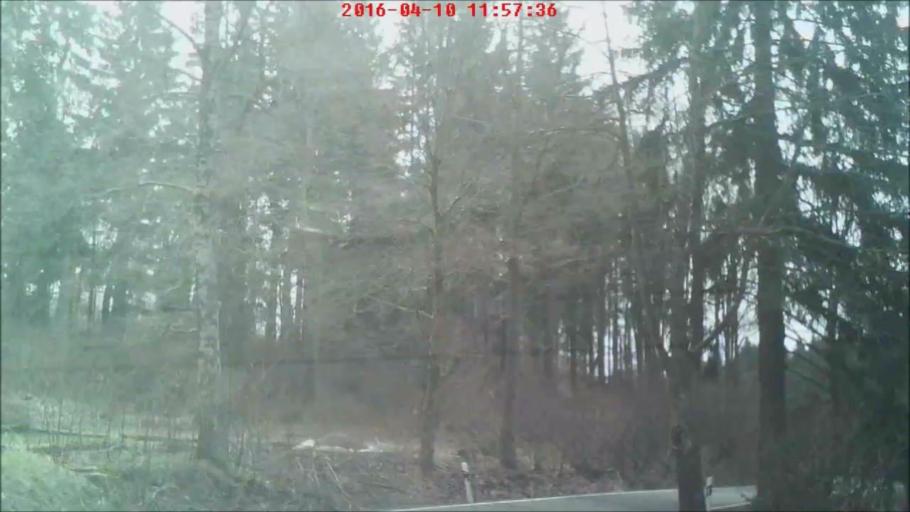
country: DE
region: Thuringia
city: Zella-Mehlis
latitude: 50.6803
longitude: 10.6488
